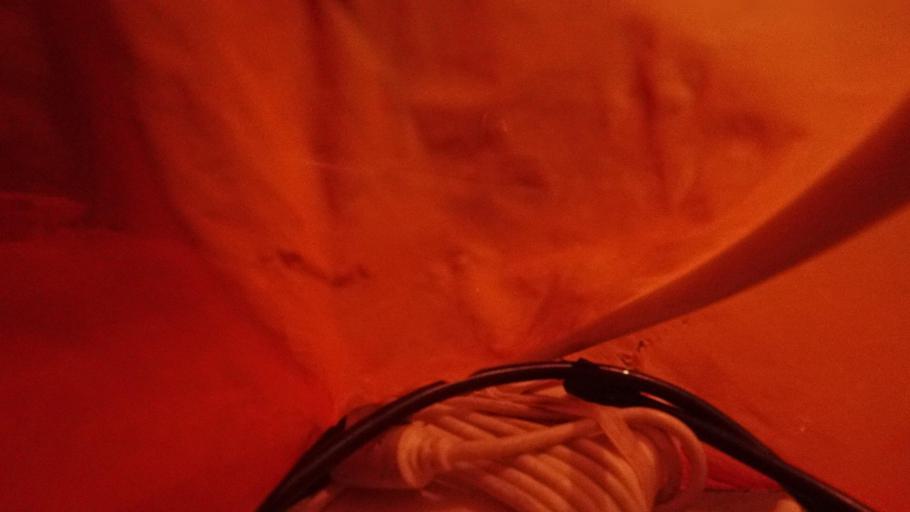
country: RU
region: Jewish Autonomous Oblast
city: Khingansk
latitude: 49.1642
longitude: 130.7620
